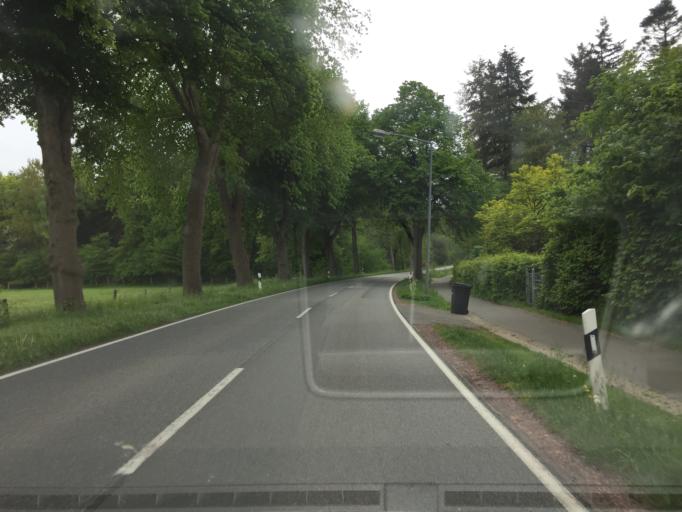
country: DE
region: Lower Saxony
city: Syke
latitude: 52.9037
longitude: 8.7979
